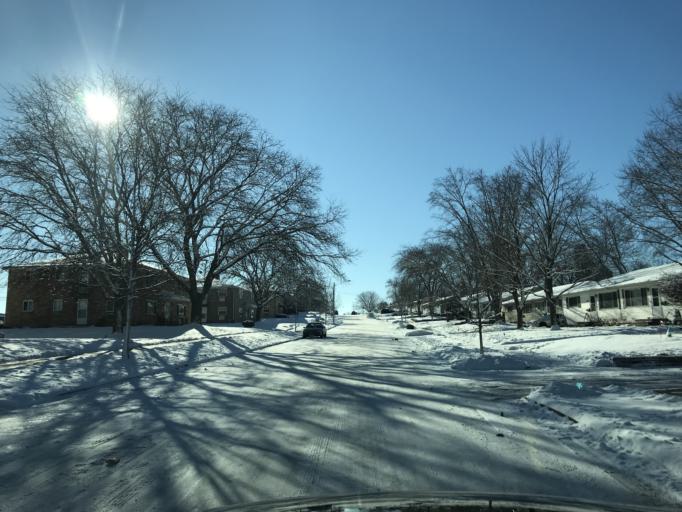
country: US
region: Wisconsin
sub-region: Dane County
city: Monona
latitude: 43.0696
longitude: -89.3118
